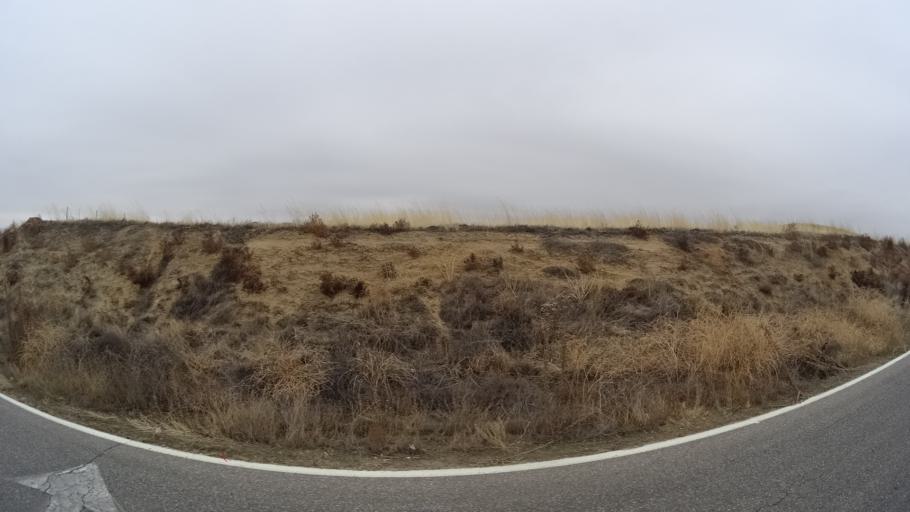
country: US
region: California
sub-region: Kern County
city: Oildale
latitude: 35.4209
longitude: -118.9482
